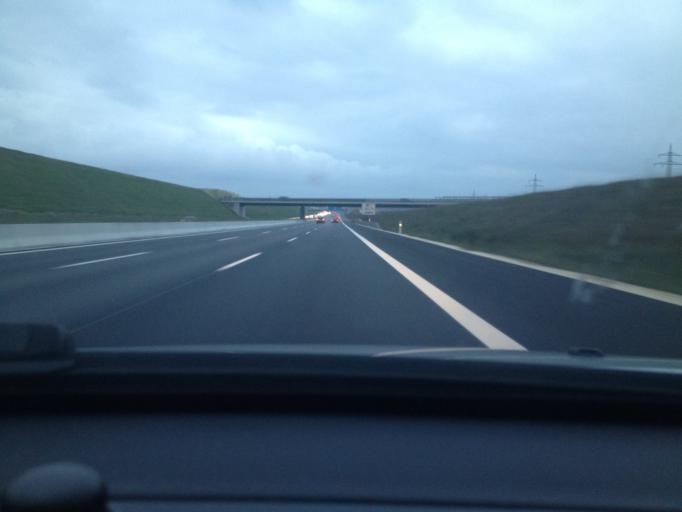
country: DE
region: Baden-Wuerttemberg
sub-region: Tuebingen Region
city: Dornstadt
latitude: 48.4616
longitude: 9.9287
